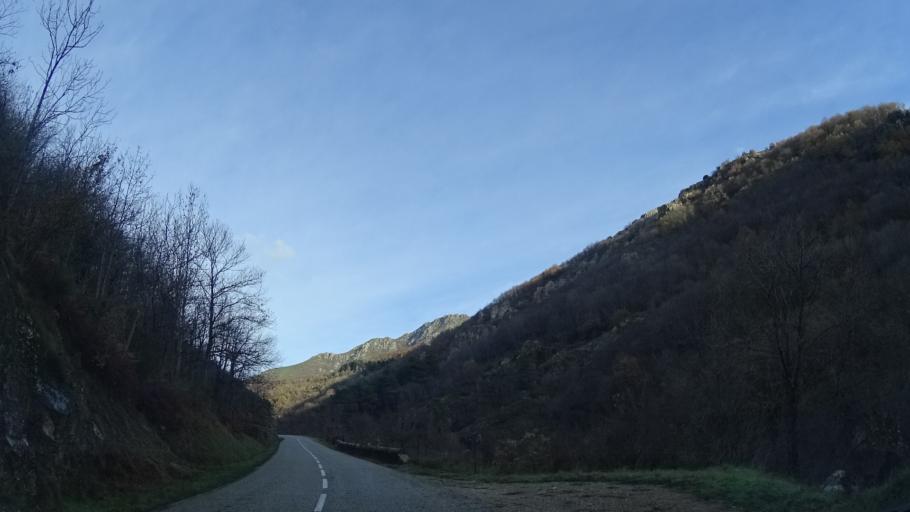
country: FR
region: Rhone-Alpes
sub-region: Departement de l'Ardeche
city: Thueyts
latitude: 44.7141
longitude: 4.2700
